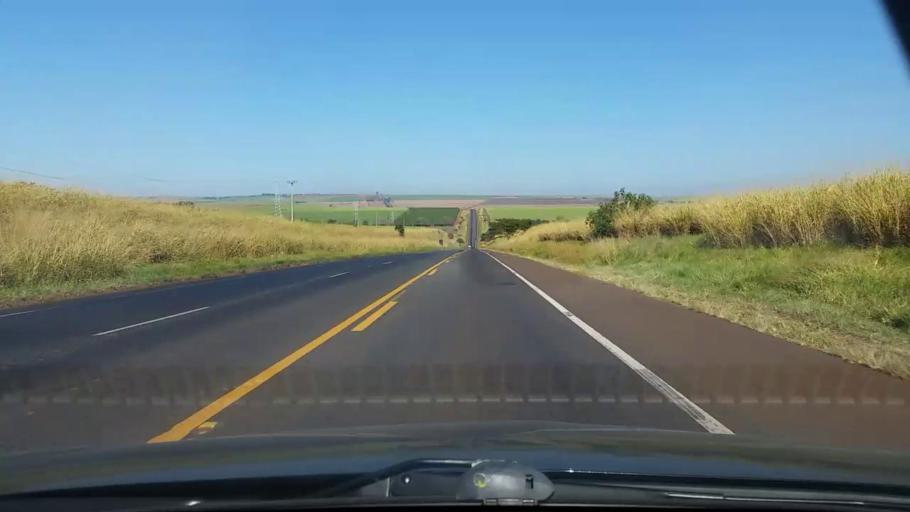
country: BR
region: Sao Paulo
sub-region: Jau
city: Jau
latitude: -22.3410
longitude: -48.5723
